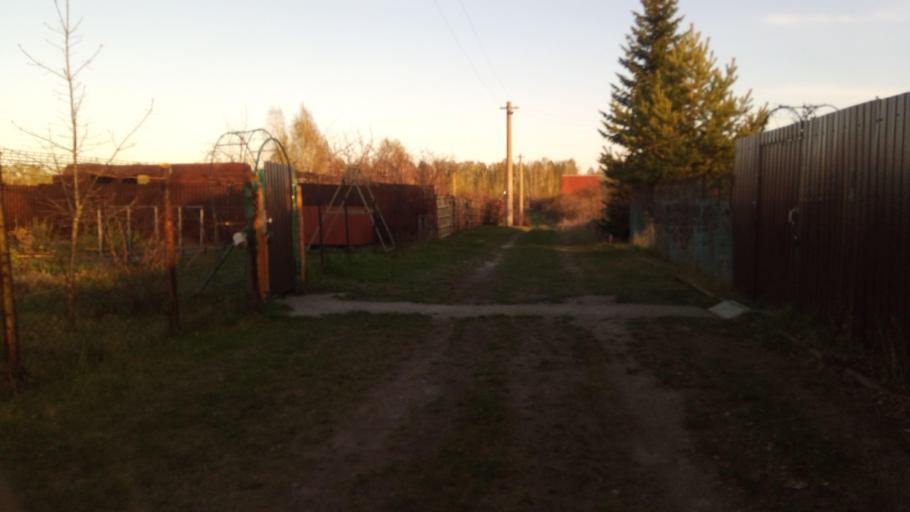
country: RU
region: Chelyabinsk
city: Timiryazevskiy
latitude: 54.9900
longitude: 60.8470
